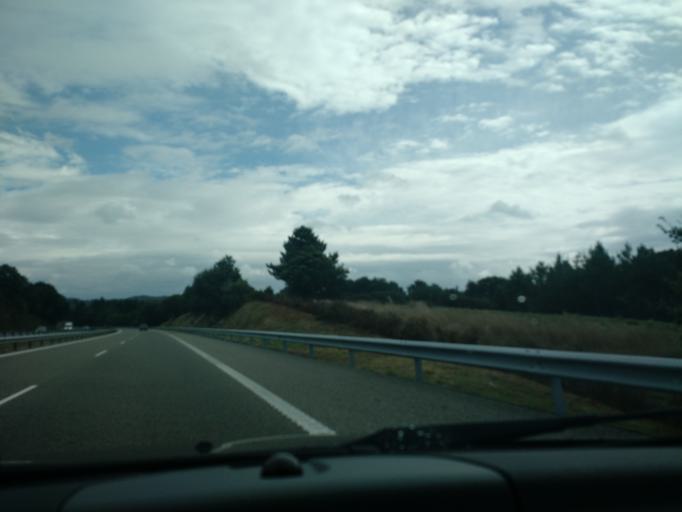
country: ES
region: Galicia
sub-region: Provincia da Coruna
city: Abegondo
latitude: 43.2307
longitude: -8.2666
